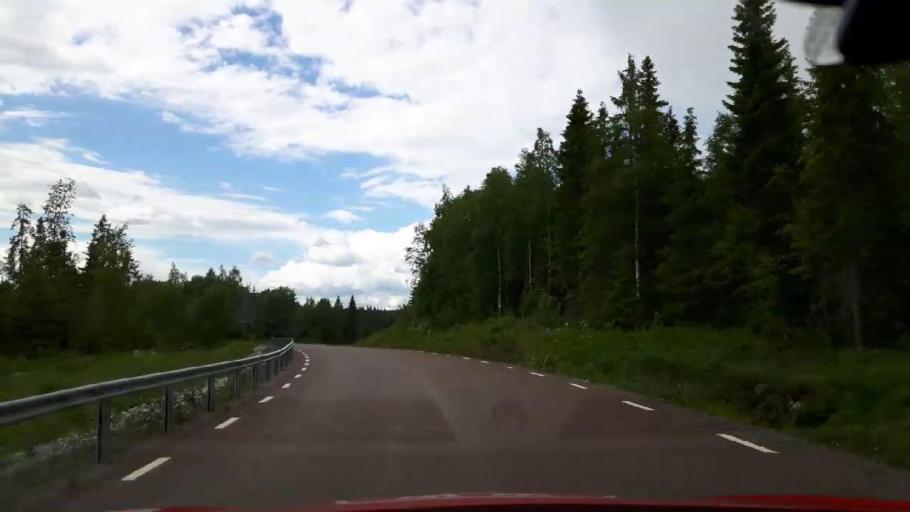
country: NO
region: Nord-Trondelag
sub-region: Lierne
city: Sandvika
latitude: 64.0900
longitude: 14.0566
